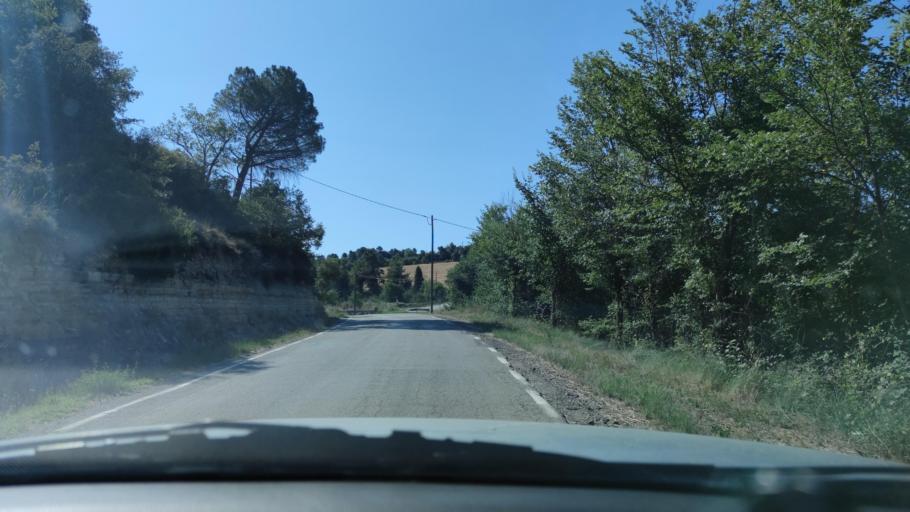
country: ES
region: Catalonia
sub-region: Provincia de Lleida
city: Sant Guim de Freixenet
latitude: 41.6806
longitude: 1.4030
